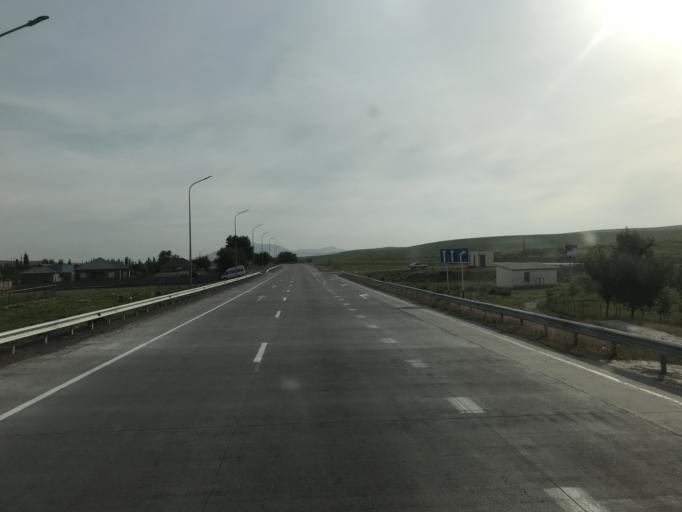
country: KZ
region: Ongtustik Qazaqstan
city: Qazyqurt
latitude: 41.8999
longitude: 69.4588
